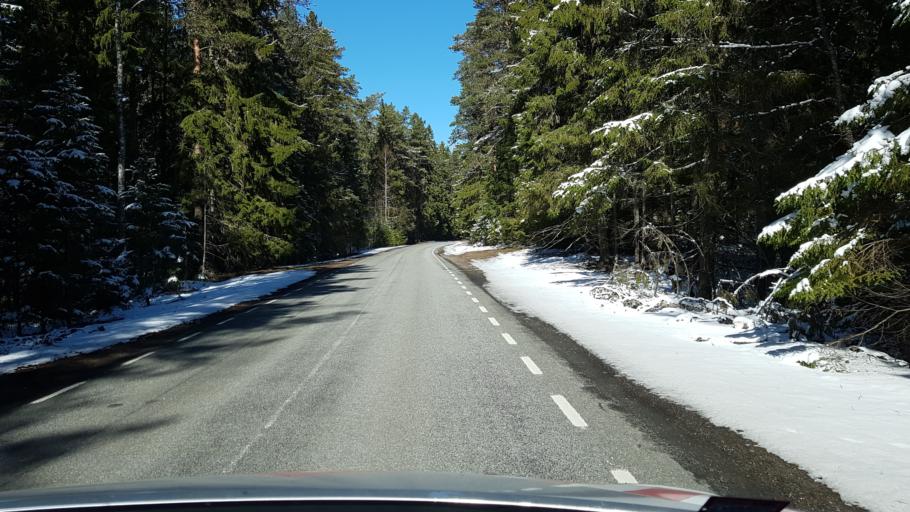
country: EE
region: Laeaene-Virumaa
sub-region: Kadrina vald
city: Kadrina
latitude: 59.4435
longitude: 26.0150
